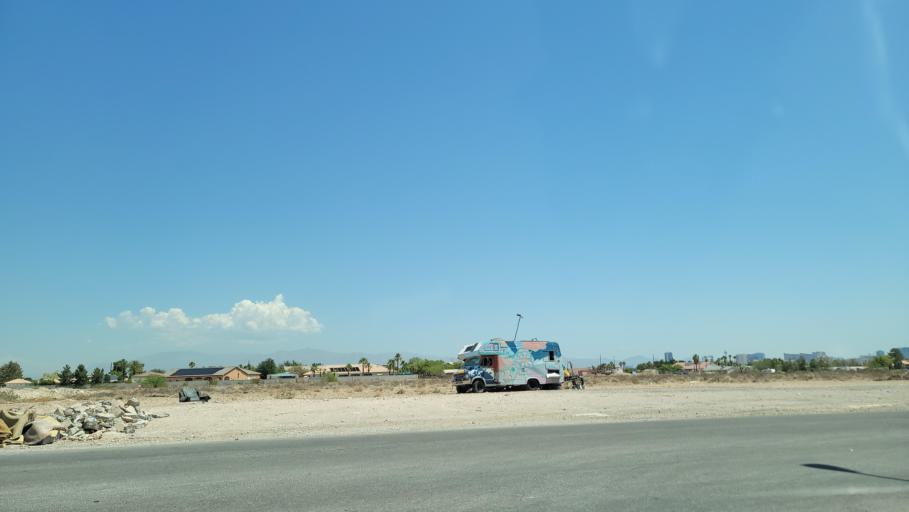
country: US
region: Nevada
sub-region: Clark County
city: Spring Valley
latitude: 36.0742
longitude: -115.2368
